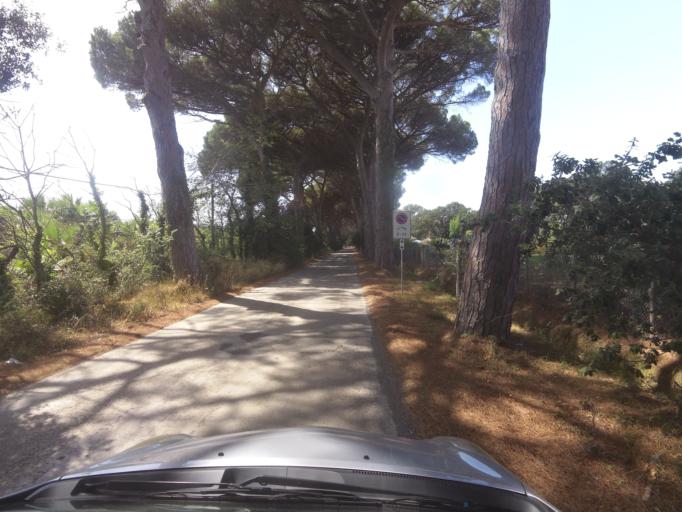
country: IT
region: Tuscany
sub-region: Provincia di Livorno
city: Donoratico
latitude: 43.1543
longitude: 10.5492
